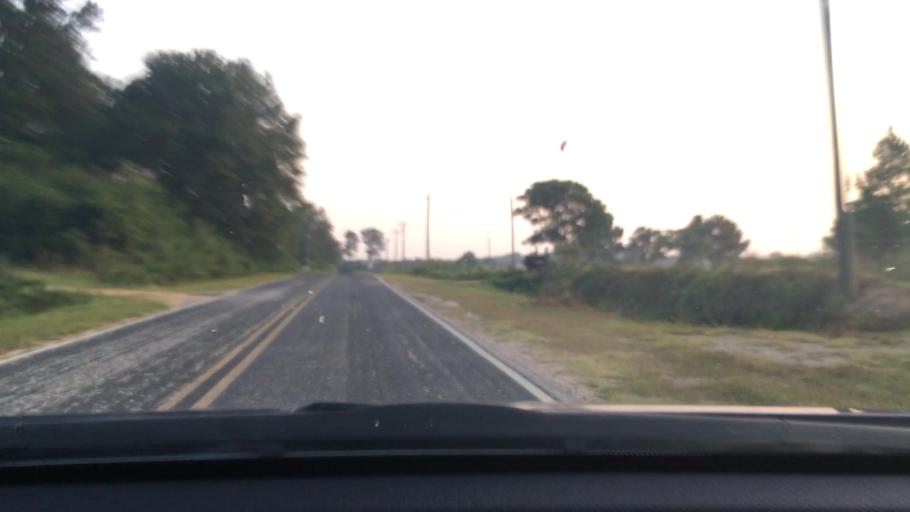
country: US
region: South Carolina
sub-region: Lee County
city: Bishopville
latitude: 34.2429
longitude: -80.1332
